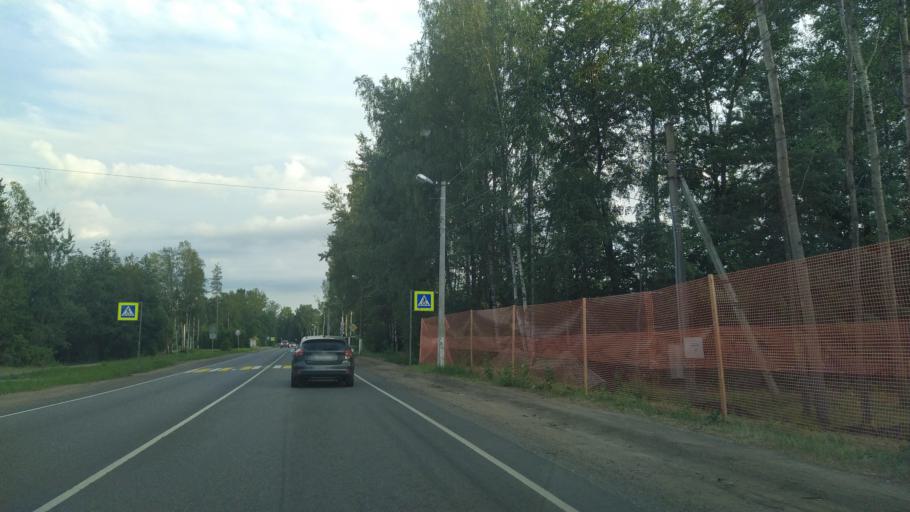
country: RU
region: Leningrad
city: Toksovo
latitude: 60.1505
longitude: 30.5222
